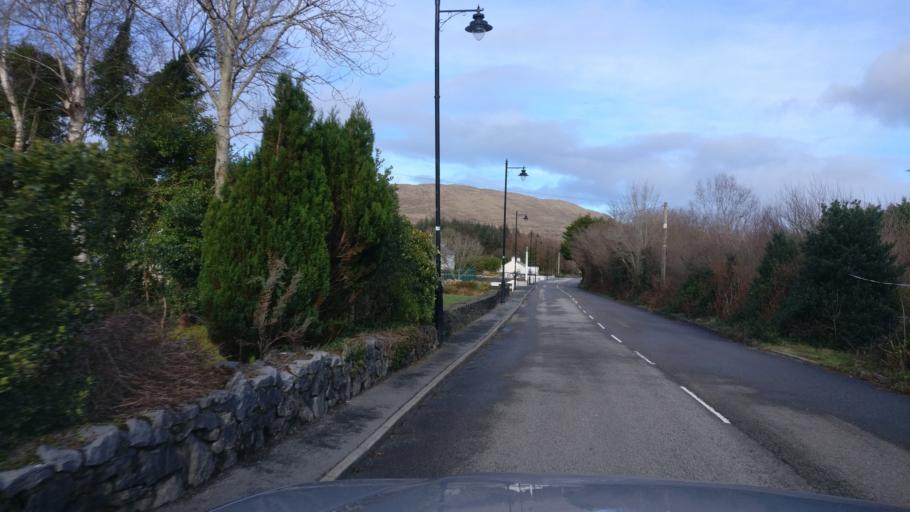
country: IE
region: Connaught
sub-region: County Galway
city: Oughterard
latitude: 53.5109
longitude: -9.4576
